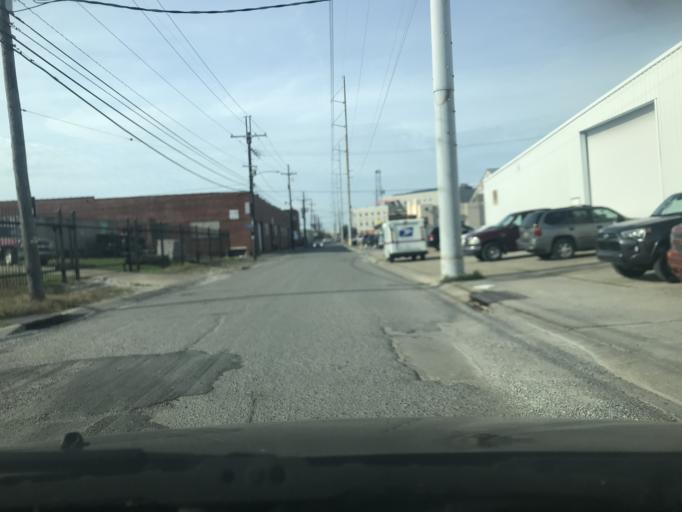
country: US
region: Louisiana
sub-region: Orleans Parish
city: New Orleans
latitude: 29.9585
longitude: -90.1000
